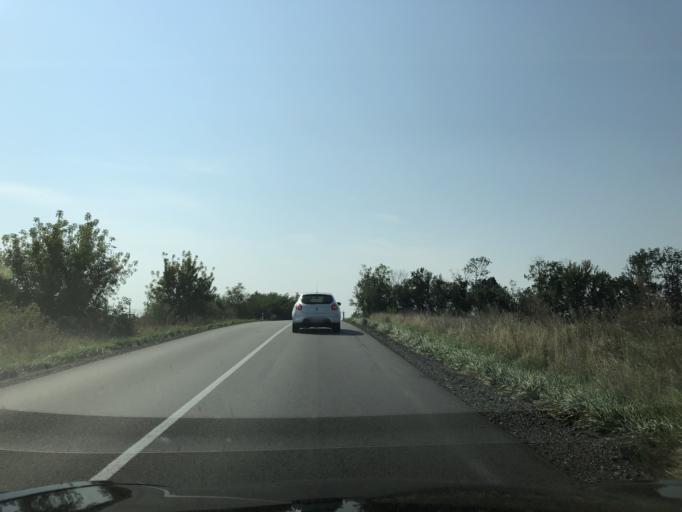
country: CZ
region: South Moravian
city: Drnholec
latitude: 48.9097
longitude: 16.5215
